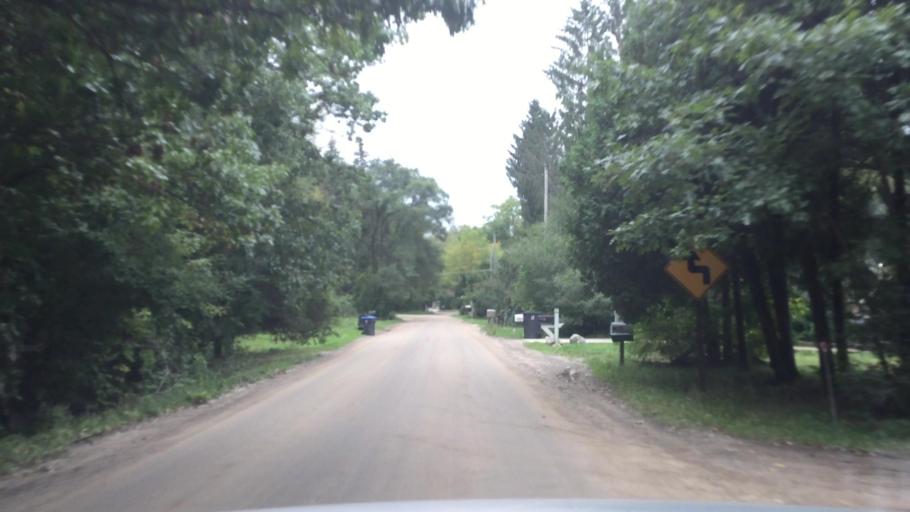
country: US
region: Michigan
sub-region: Livingston County
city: Whitmore Lake
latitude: 42.4705
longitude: -83.7958
